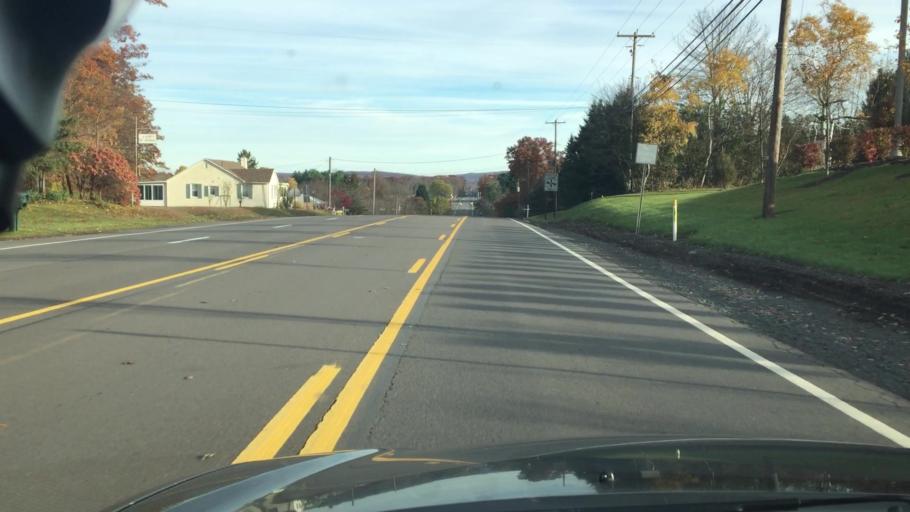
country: US
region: Pennsylvania
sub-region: Luzerne County
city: Mountain Top
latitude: 41.1221
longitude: -75.9091
